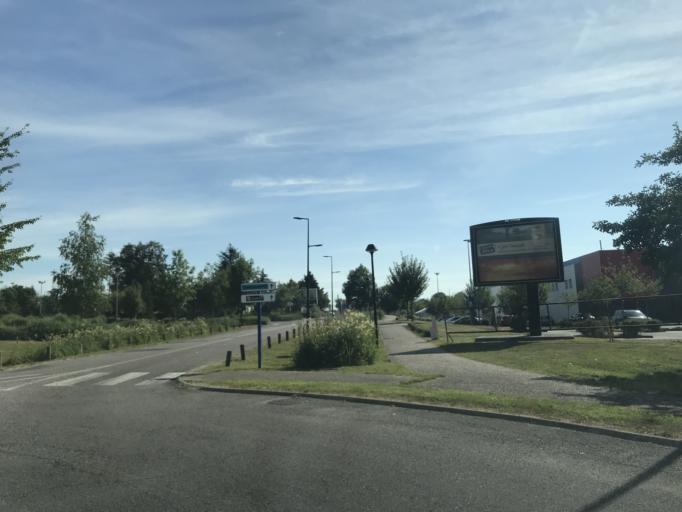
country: FR
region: Haute-Normandie
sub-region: Departement de la Seine-Maritime
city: Roumare
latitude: 49.5268
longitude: 0.9659
